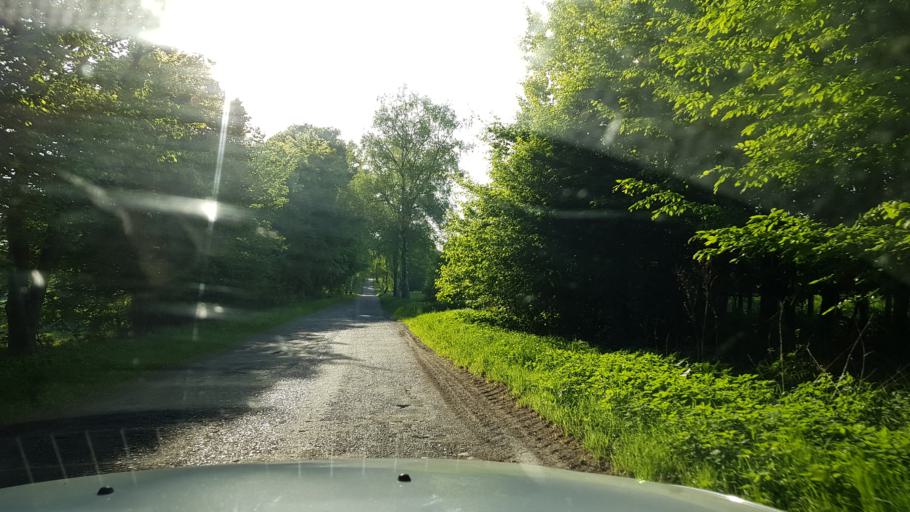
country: PL
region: West Pomeranian Voivodeship
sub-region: Powiat lobeski
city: Dobra
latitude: 53.6350
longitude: 15.3719
